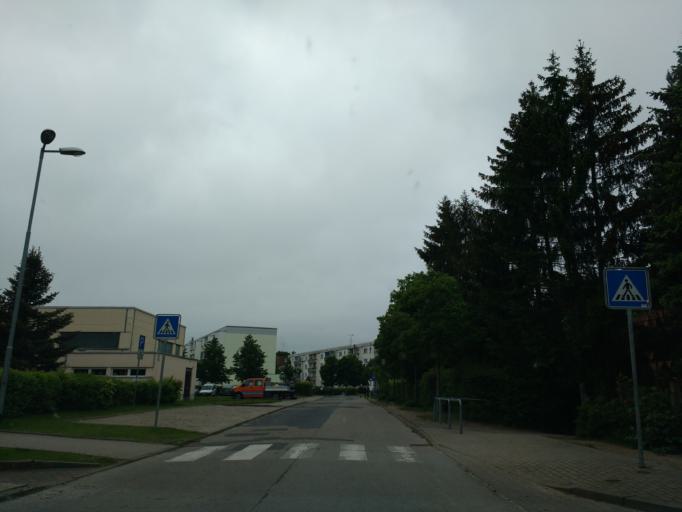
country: DE
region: Mecklenburg-Vorpommern
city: Neukloster
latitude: 53.8618
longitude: 11.6934
